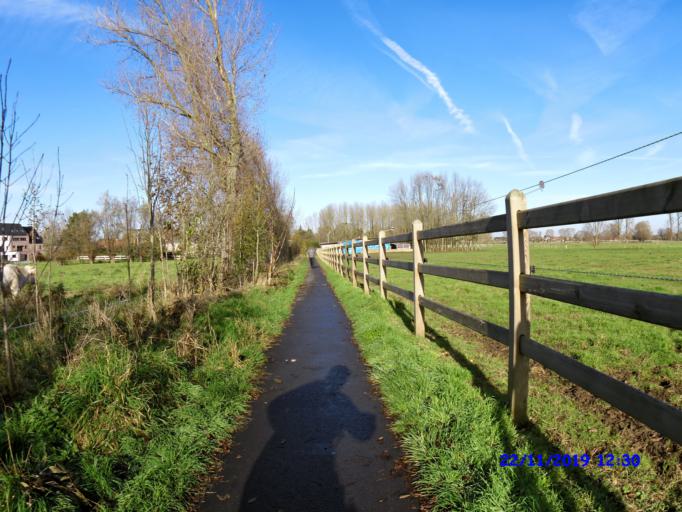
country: BE
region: Flanders
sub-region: Provincie Vlaams-Brabant
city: Merchtem
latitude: 50.9618
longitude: 4.2334
